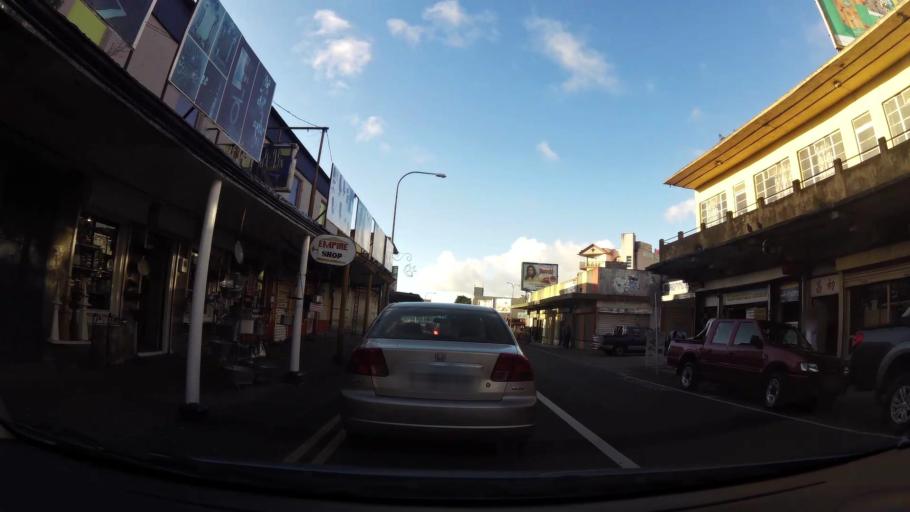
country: MU
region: Plaines Wilhems
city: Curepipe
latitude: -20.3146
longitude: 57.5233
